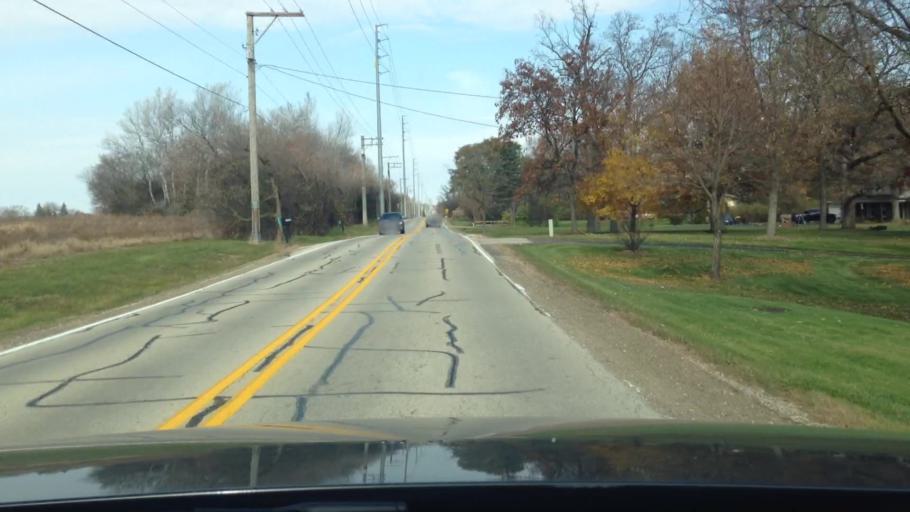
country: US
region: Illinois
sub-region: McHenry County
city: Woodstock
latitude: 42.2704
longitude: -88.4525
